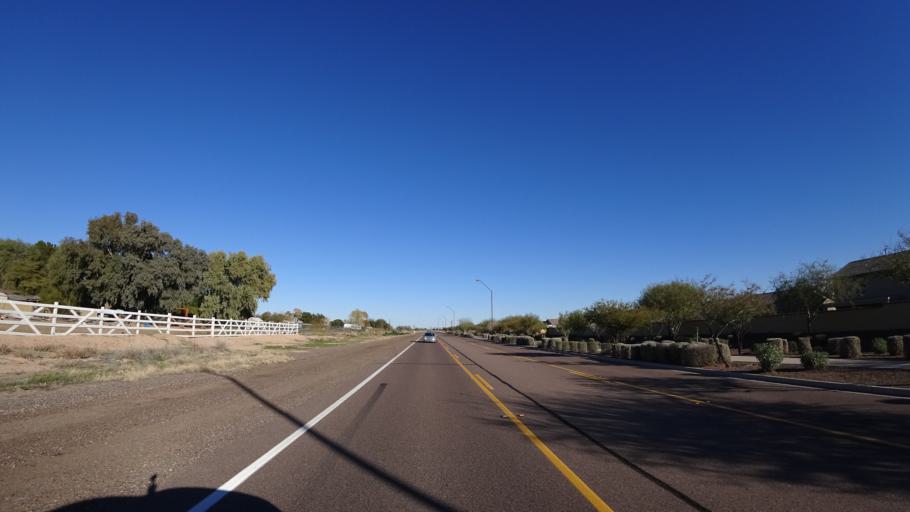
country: US
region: Arizona
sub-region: Maricopa County
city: Citrus Park
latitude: 33.4502
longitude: -112.4735
